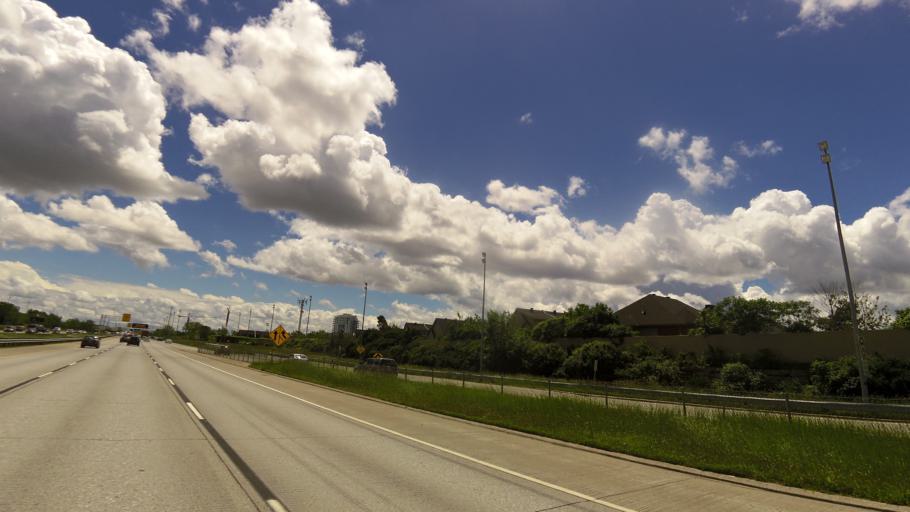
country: CA
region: Quebec
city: Dollard-Des Ormeaux
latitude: 45.5210
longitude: -73.7744
